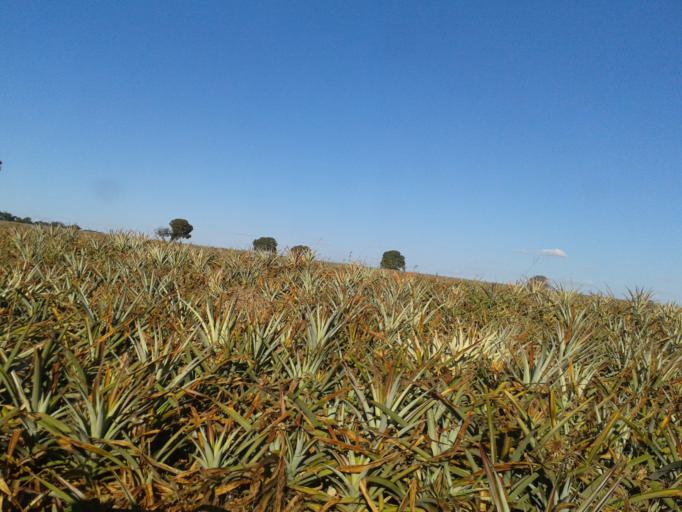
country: BR
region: Minas Gerais
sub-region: Centralina
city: Centralina
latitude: -18.7512
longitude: -49.1007
